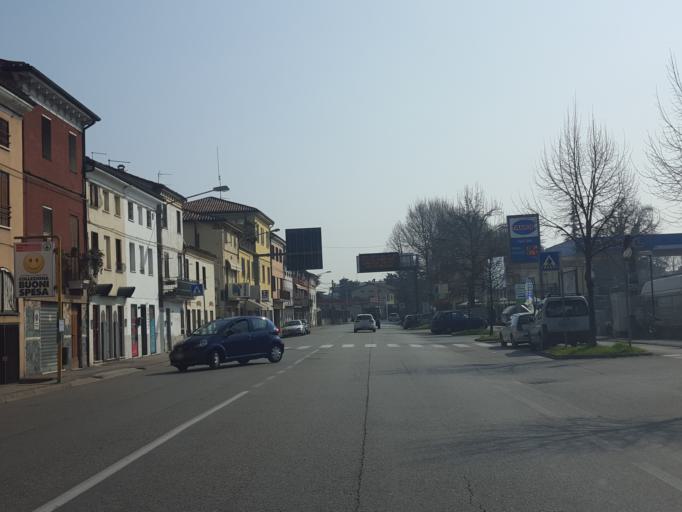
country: IT
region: Veneto
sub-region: Provincia di Vicenza
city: Vicenza
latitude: 45.5575
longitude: 11.5249
